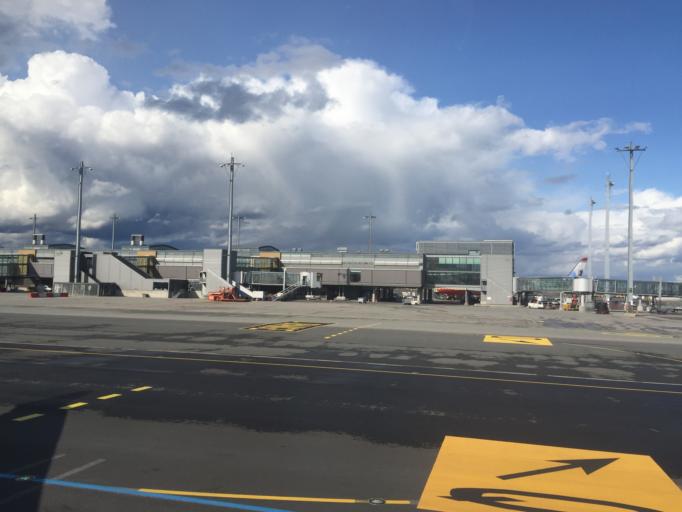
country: NO
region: Akershus
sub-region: Ullensaker
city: Jessheim
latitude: 60.1918
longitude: 11.1064
